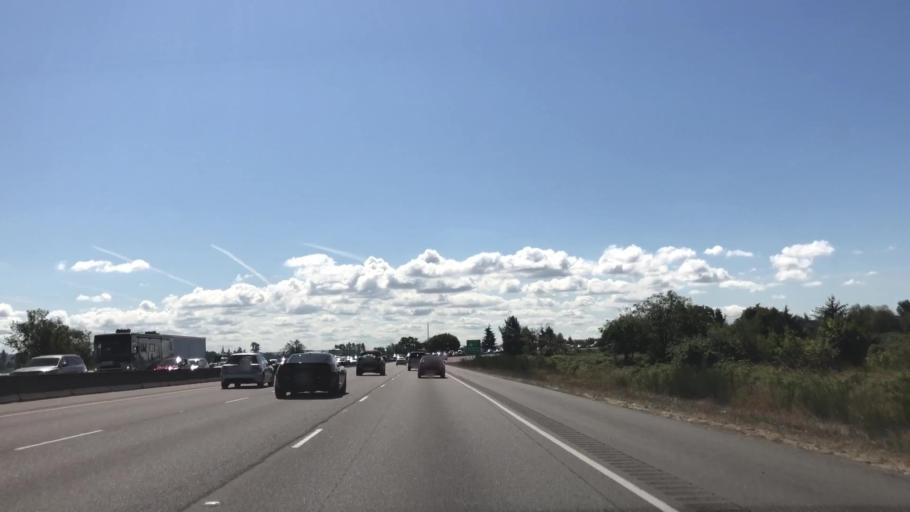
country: US
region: Washington
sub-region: Snohomish County
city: Everett
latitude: 48.0006
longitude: -122.1754
